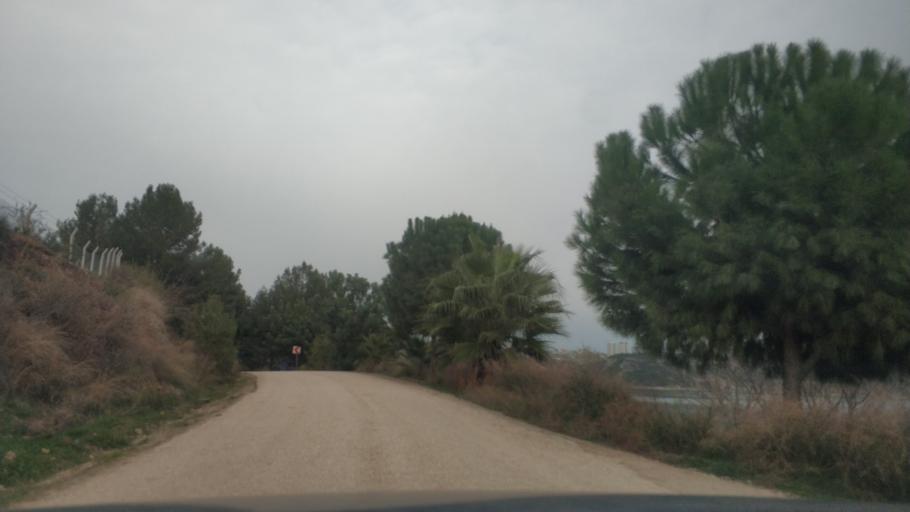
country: TR
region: Adana
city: Adana
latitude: 37.0764
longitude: 35.3247
